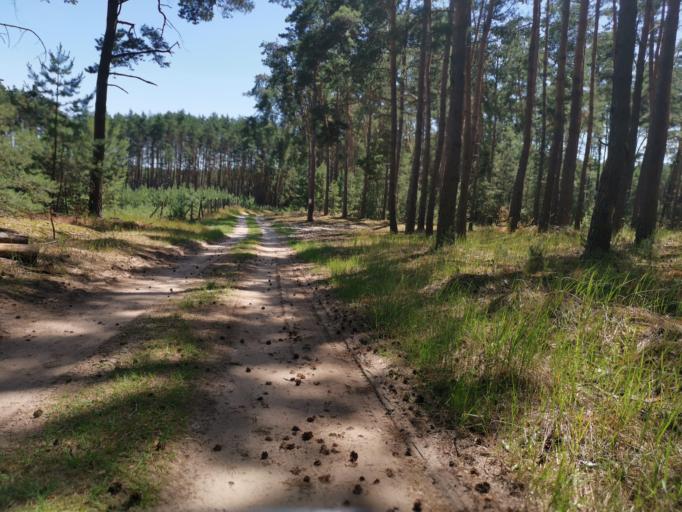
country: CZ
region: South Moravian
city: Vracov
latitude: 48.9521
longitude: 17.2285
